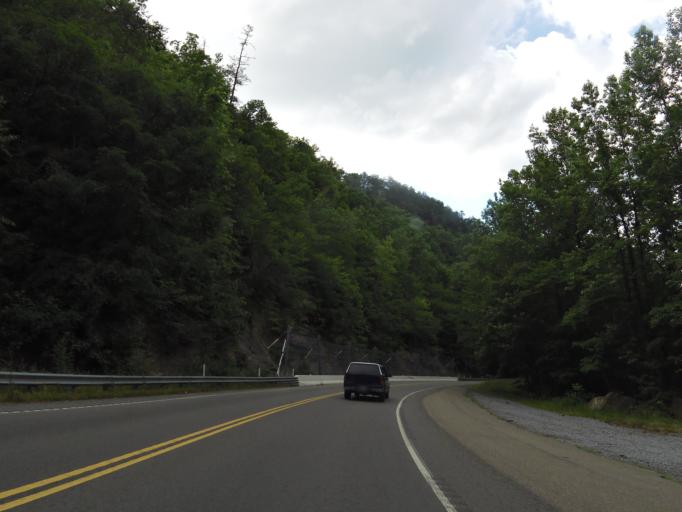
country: US
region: Tennessee
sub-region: Blount County
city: Wildwood
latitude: 35.6925
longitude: -83.8005
